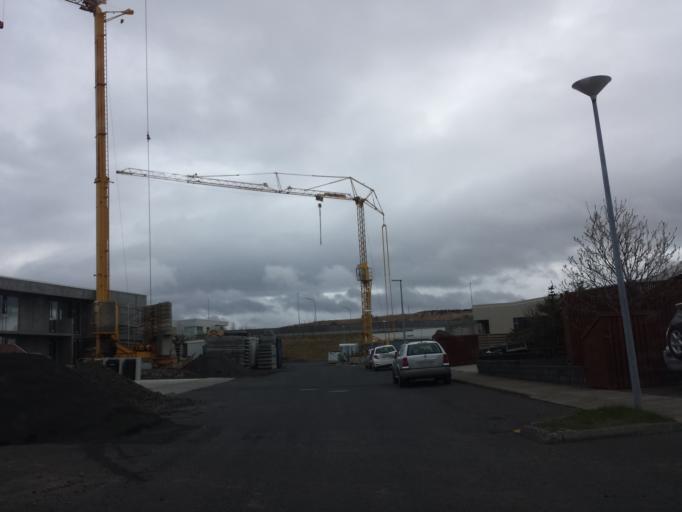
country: IS
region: Capital Region
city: Kopavogur
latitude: 64.0951
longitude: -21.8924
